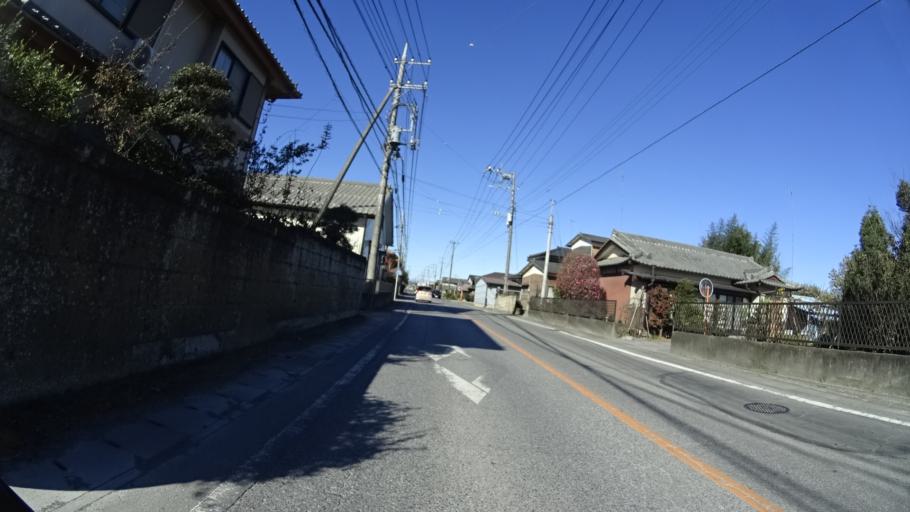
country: JP
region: Tochigi
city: Mibu
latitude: 36.4499
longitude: 139.7564
